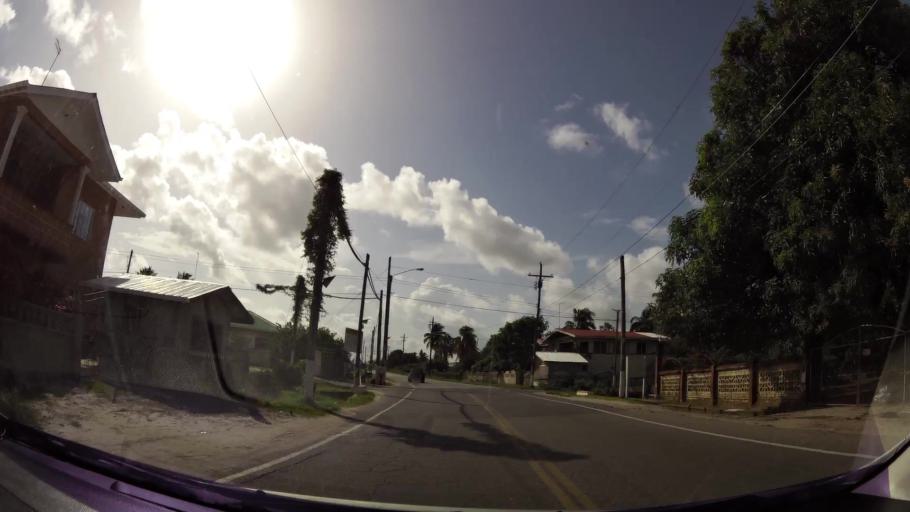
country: GY
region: Demerara-Mahaica
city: Mahaica Village
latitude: 6.7482
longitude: -57.9659
